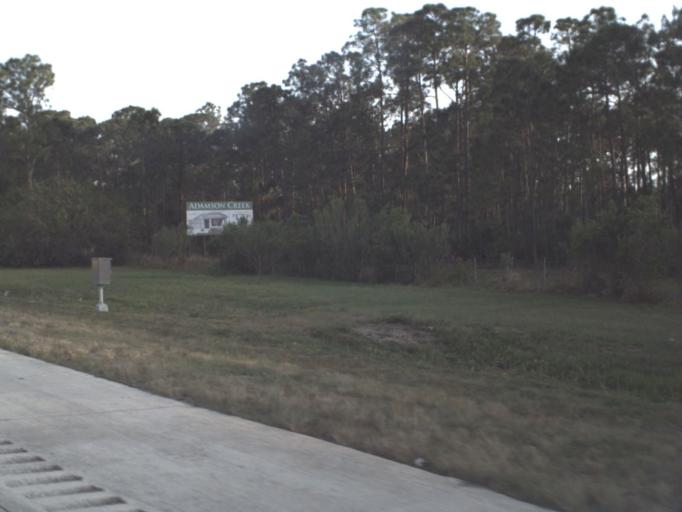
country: US
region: Florida
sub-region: Brevard County
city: Cocoa West
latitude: 28.3857
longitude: -80.8119
